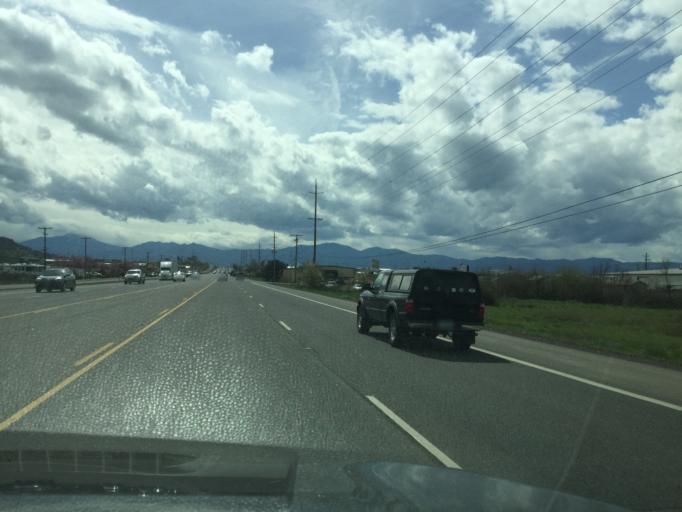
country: US
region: Oregon
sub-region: Jackson County
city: White City
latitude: 42.3969
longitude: -122.8561
